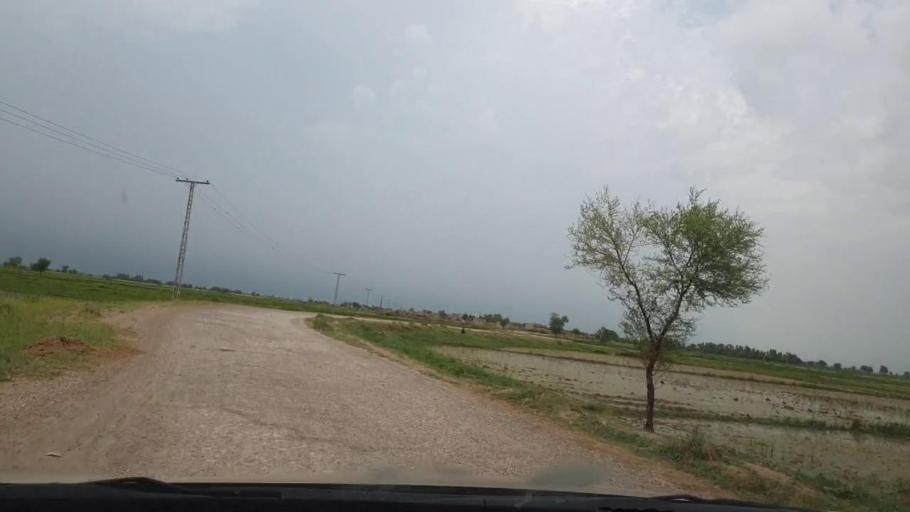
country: PK
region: Sindh
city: Ratodero
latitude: 27.8151
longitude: 68.3170
